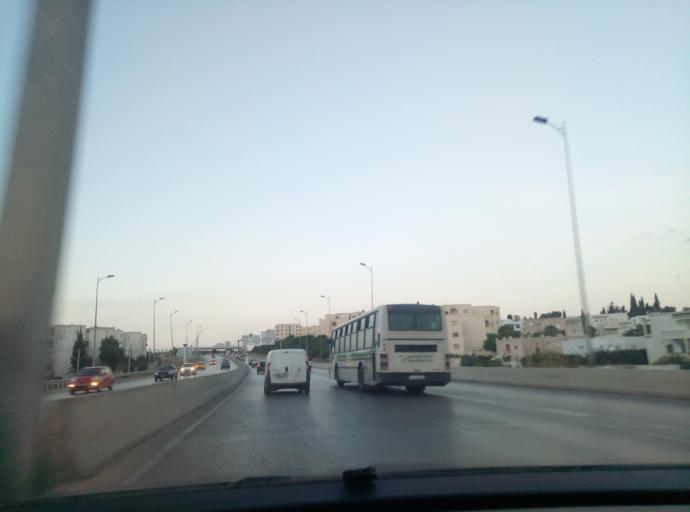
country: TN
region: Tunis
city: Tunis
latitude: 36.8227
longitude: 10.1404
